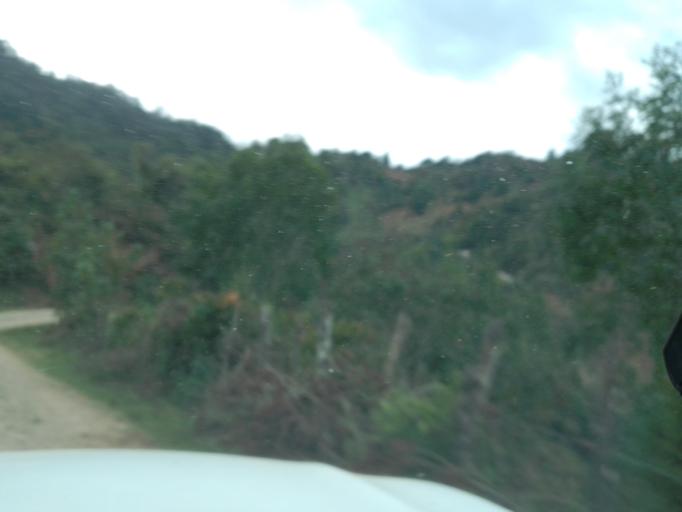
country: MX
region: Chiapas
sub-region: Cacahoatan
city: Benito Juarez
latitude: 15.2085
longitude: -92.2230
